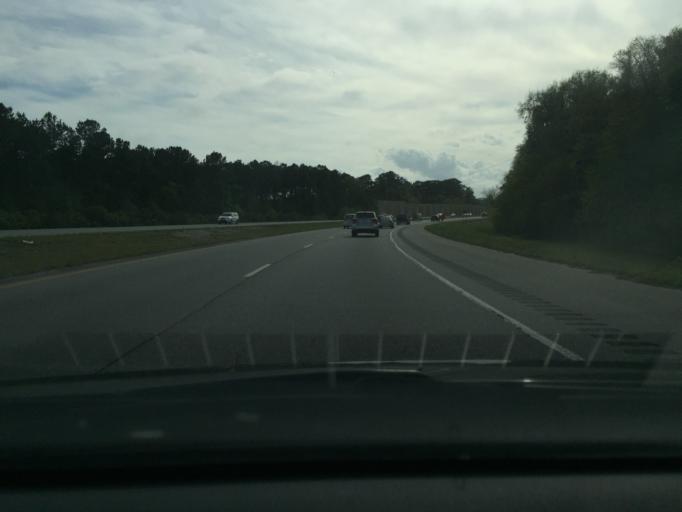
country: US
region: Georgia
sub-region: Chatham County
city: Isle of Hope
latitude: 31.9756
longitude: -81.0970
